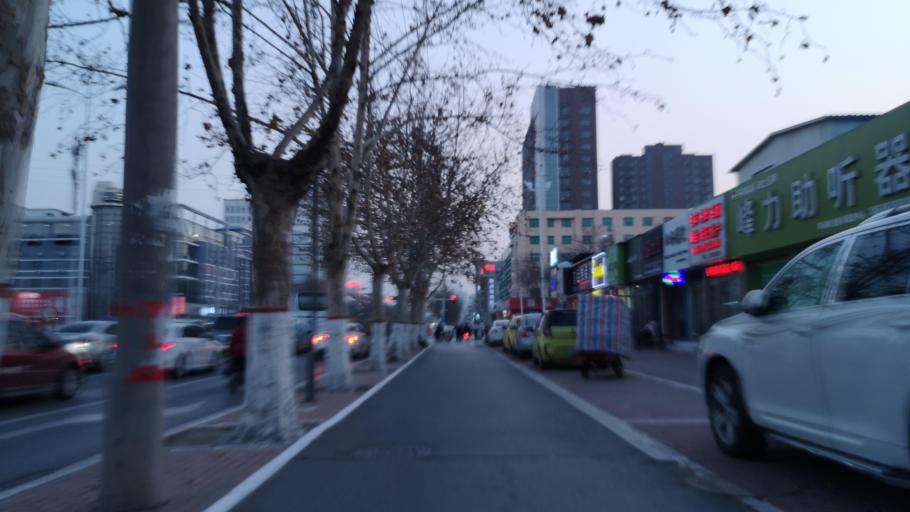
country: CN
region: Henan Sheng
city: Zhongyuanlu
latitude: 35.7698
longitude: 115.0691
